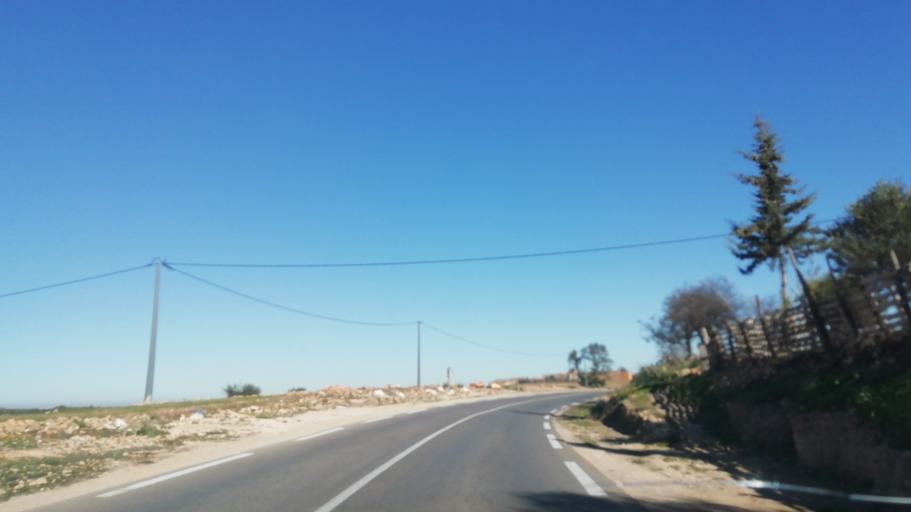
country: DZ
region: Tlemcen
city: Beni Mester
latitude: 34.8235
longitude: -1.6113
